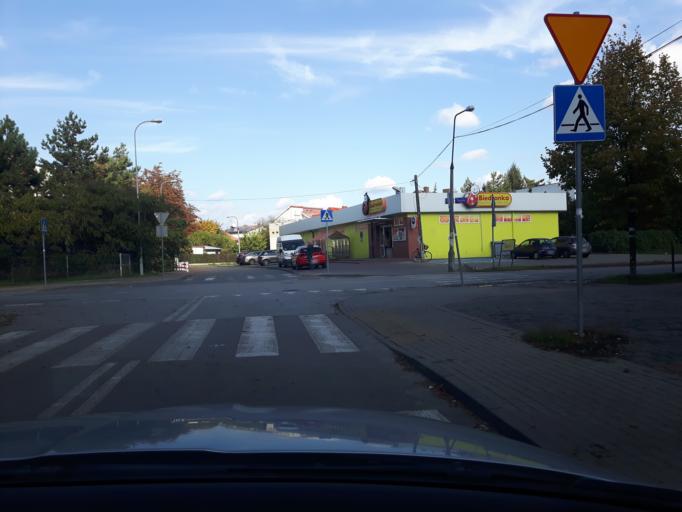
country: PL
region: Masovian Voivodeship
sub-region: Powiat wolominski
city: Zabki
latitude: 52.2811
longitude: 21.0786
